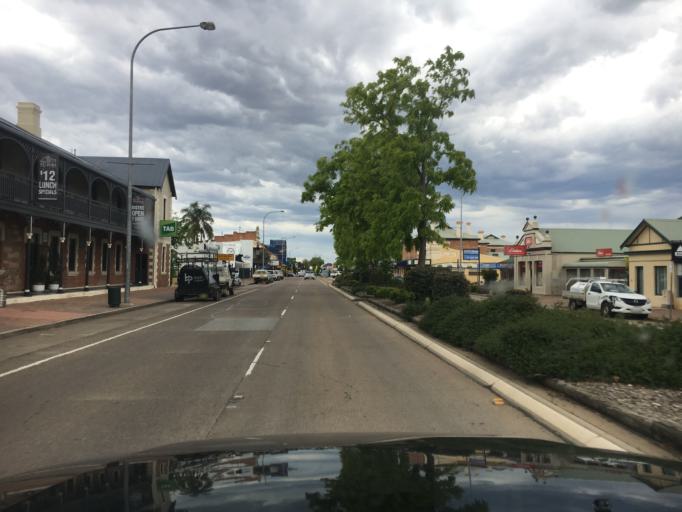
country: AU
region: New South Wales
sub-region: Muswellbrook
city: Muswellbrook
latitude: -32.0472
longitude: 150.8682
